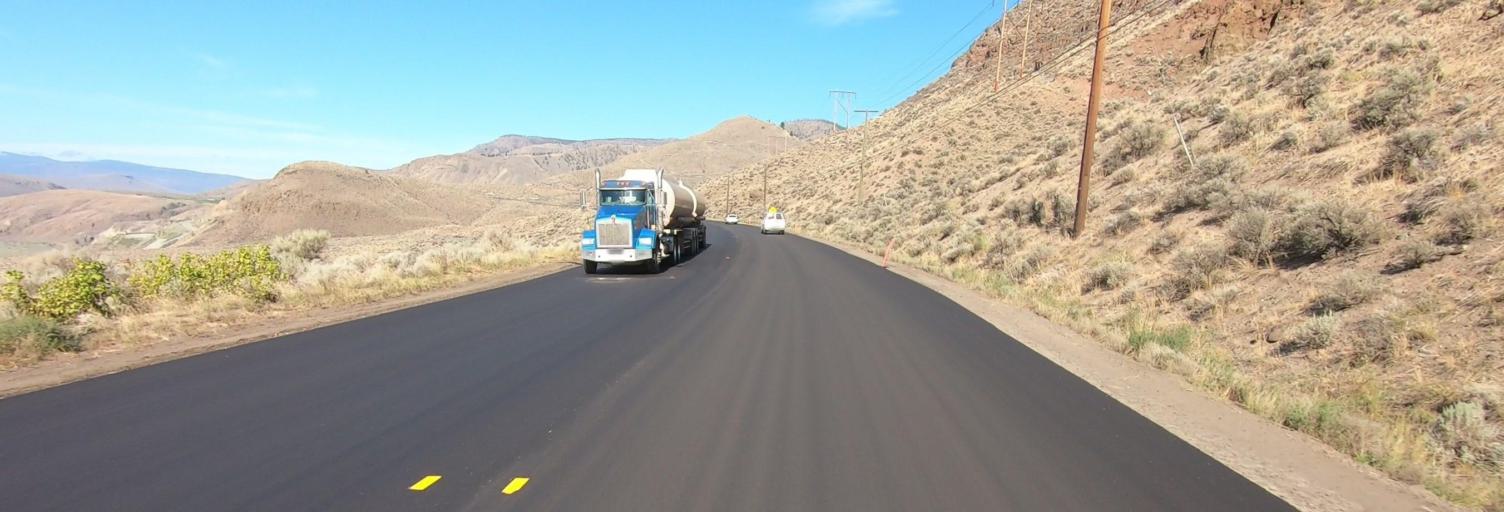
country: CA
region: British Columbia
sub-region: Thompson-Nicola Regional District
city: Ashcroft
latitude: 50.7947
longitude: -121.0919
